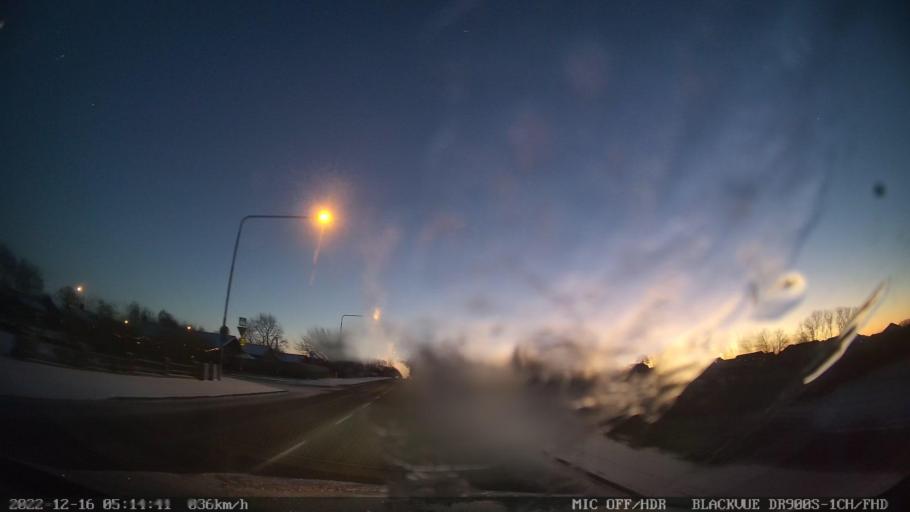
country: SE
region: Skane
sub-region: Tomelilla Kommun
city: Tomelilla
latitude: 55.5389
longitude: 13.9428
